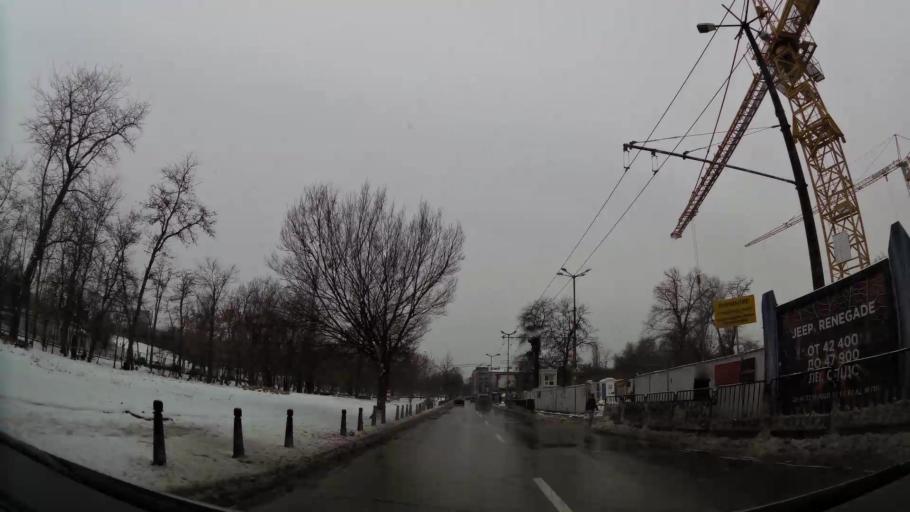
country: BG
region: Sofia-Capital
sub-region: Stolichna Obshtina
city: Sofia
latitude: 42.6904
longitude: 23.3366
